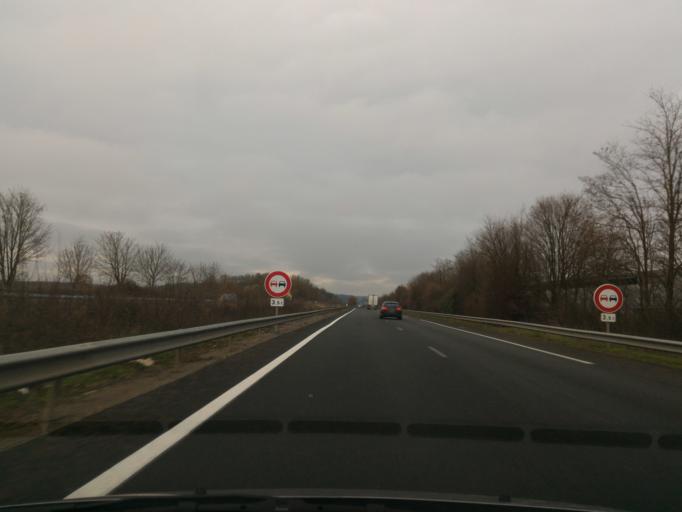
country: FR
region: Poitou-Charentes
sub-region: Departement de la Vienne
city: Fontaine-le-Comte
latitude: 46.5048
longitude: 0.2777
